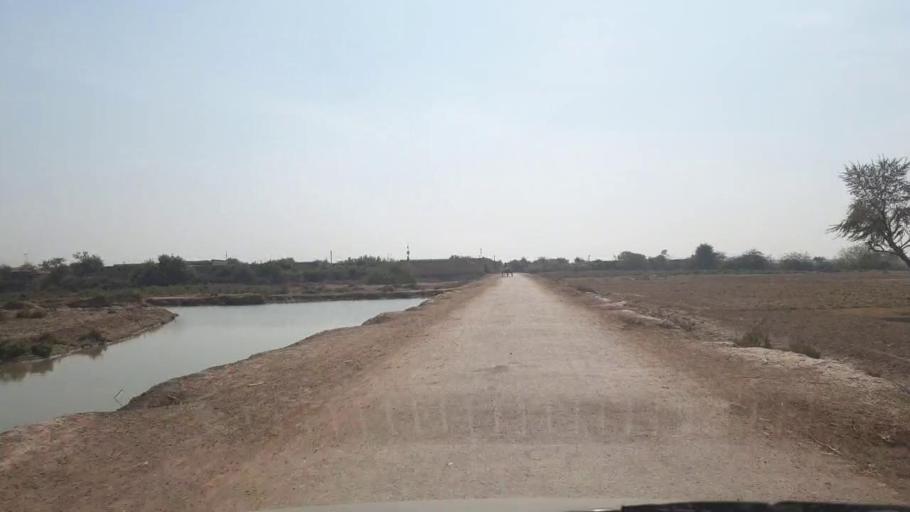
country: PK
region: Sindh
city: Chambar
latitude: 25.3407
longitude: 68.8117
